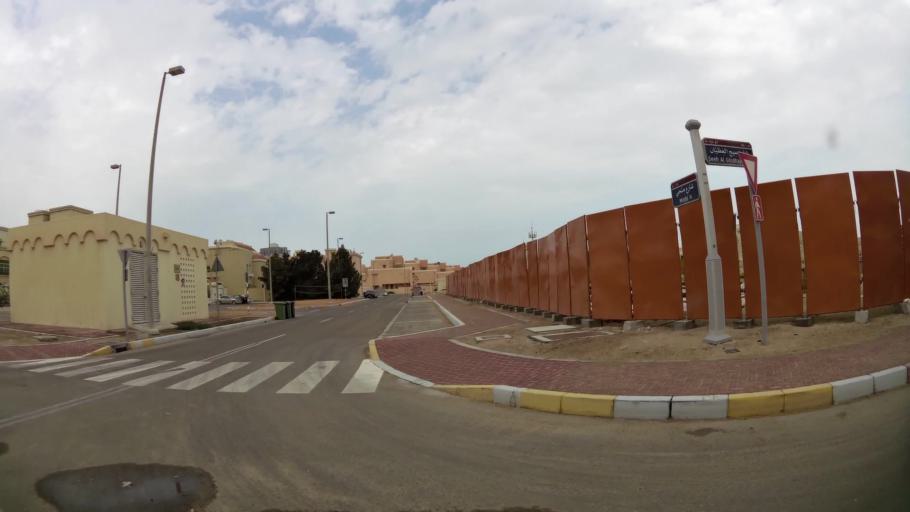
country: AE
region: Abu Dhabi
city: Abu Dhabi
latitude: 24.4286
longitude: 54.4457
